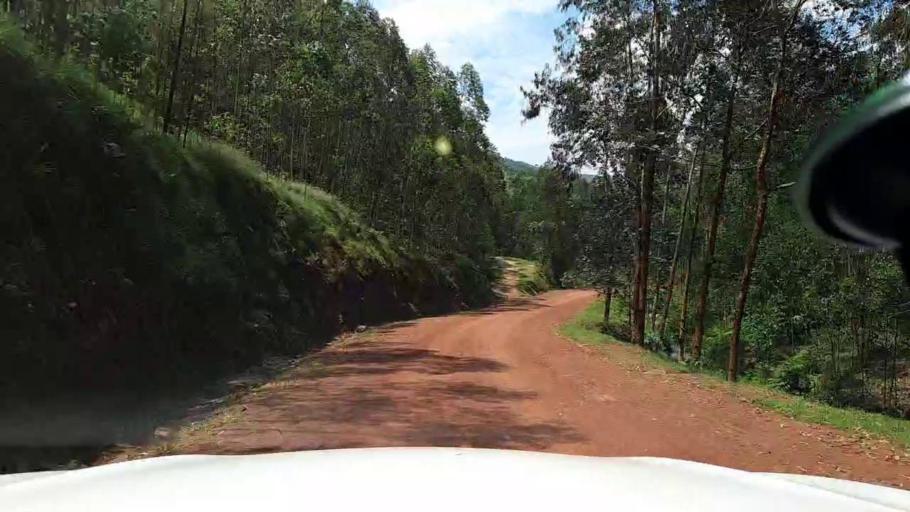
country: RW
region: Northern Province
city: Byumba
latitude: -1.7050
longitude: 29.8448
